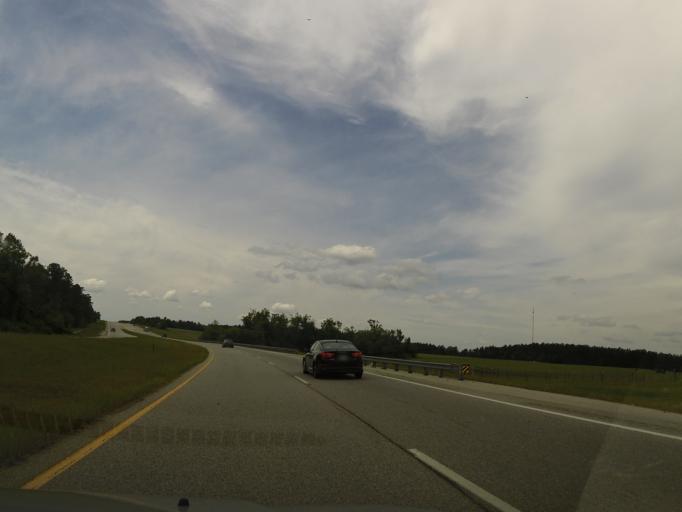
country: US
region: Georgia
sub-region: Emanuel County
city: Swainsboro
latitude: 32.5316
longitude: -82.3029
